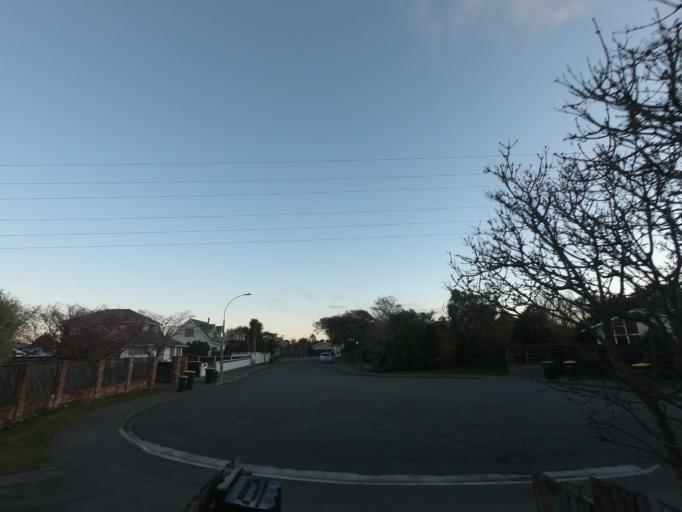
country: NZ
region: Canterbury
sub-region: Selwyn District
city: Prebbleton
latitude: -43.5729
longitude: 172.5647
